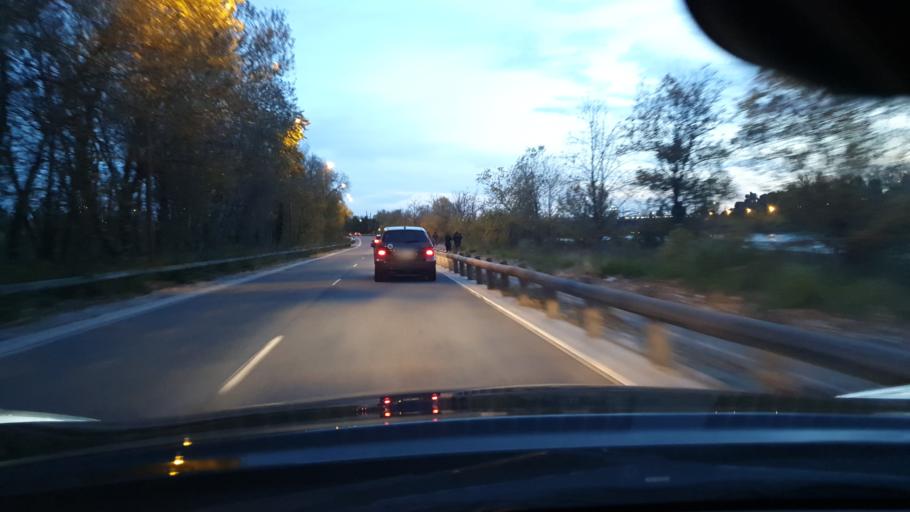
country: FR
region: Provence-Alpes-Cote d'Azur
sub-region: Departement des Alpes-Maritimes
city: Saint-Laurent-du-Var
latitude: 43.6680
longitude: 7.1985
